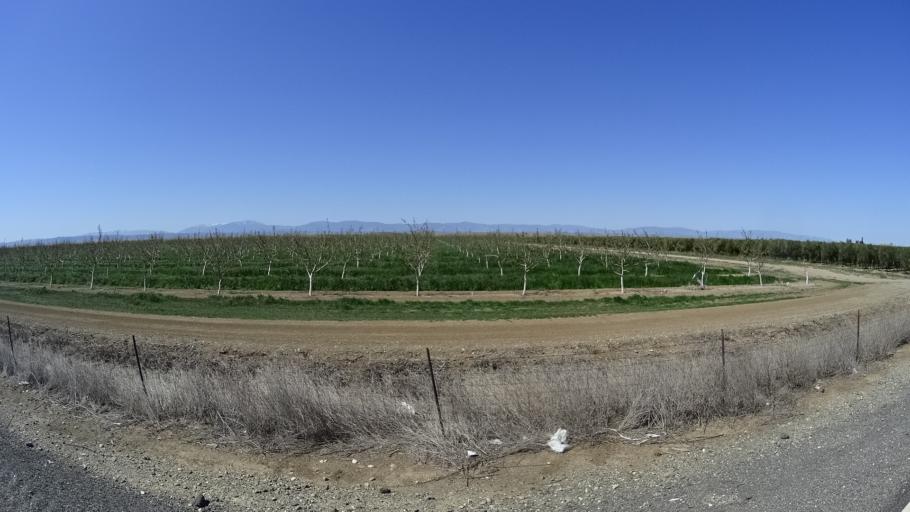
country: US
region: California
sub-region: Glenn County
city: Willows
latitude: 39.5894
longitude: -122.2498
